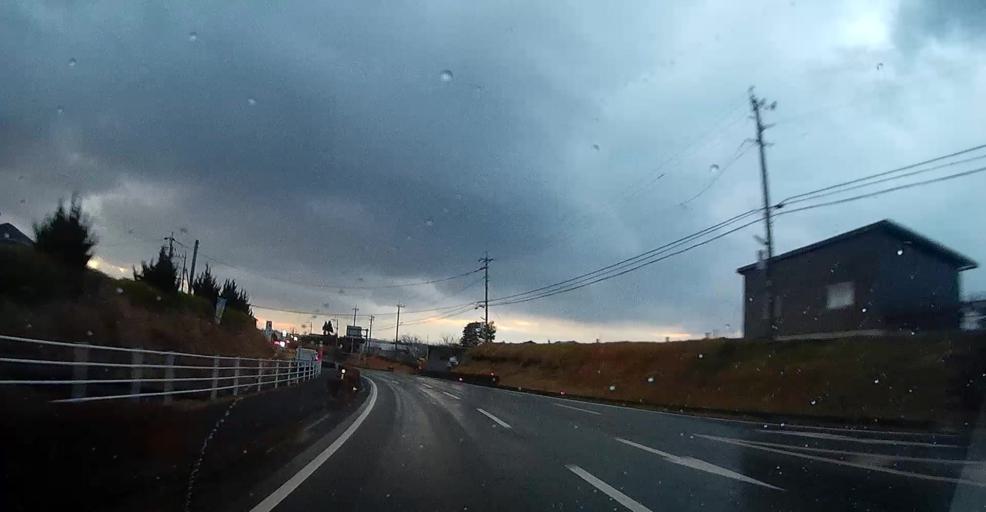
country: JP
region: Kumamoto
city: Ozu
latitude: 32.8394
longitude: 130.9089
